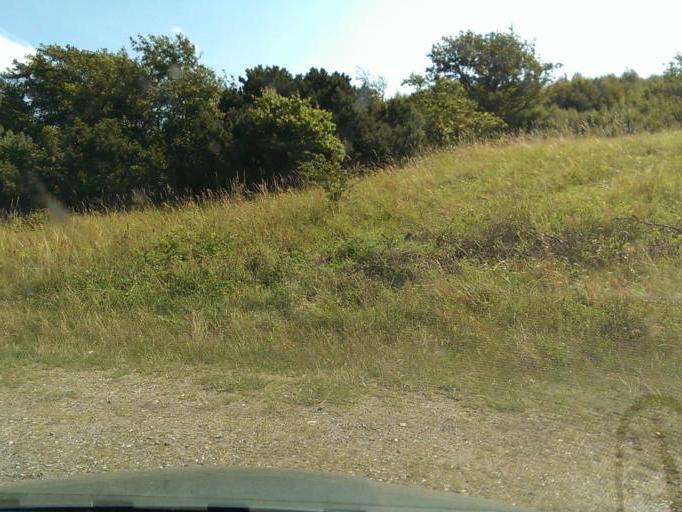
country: DK
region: Central Jutland
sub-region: Syddjurs Kommune
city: Ebeltoft
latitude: 56.1188
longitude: 10.5236
